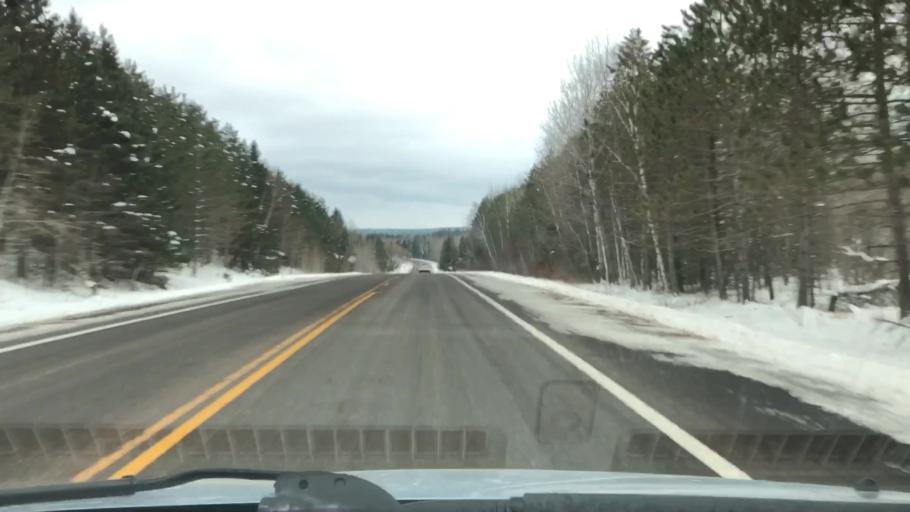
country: US
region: Minnesota
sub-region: Carlton County
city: Esko
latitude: 46.6768
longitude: -92.3762
